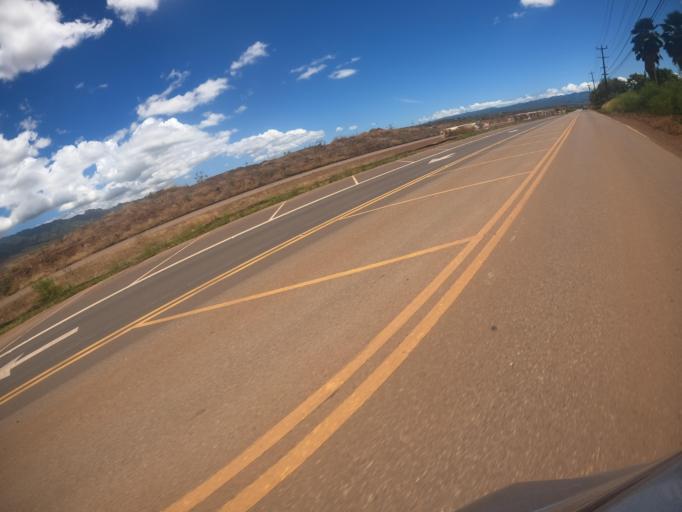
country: US
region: Hawaii
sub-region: Honolulu County
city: Royal Kunia
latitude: 21.3729
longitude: -158.0432
